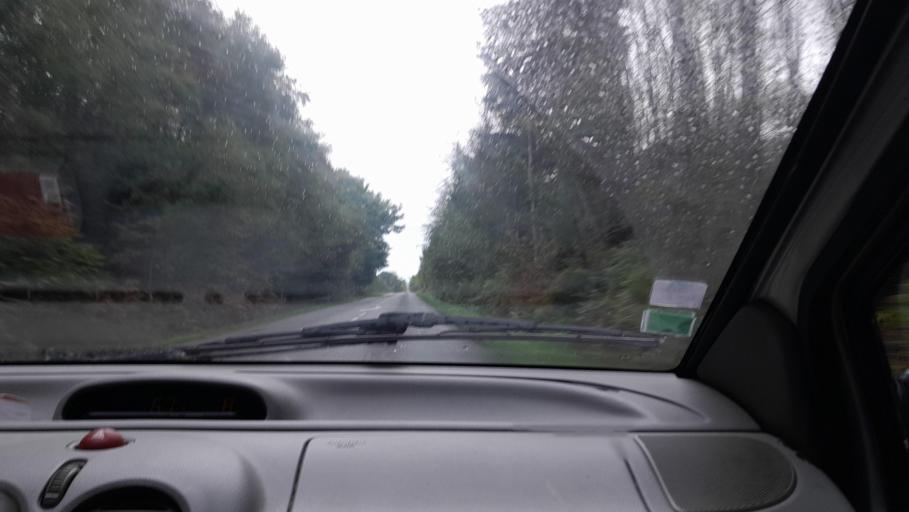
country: FR
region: Pays de la Loire
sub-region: Departement de la Mayenne
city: Congrier
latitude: 47.8829
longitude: -1.1240
